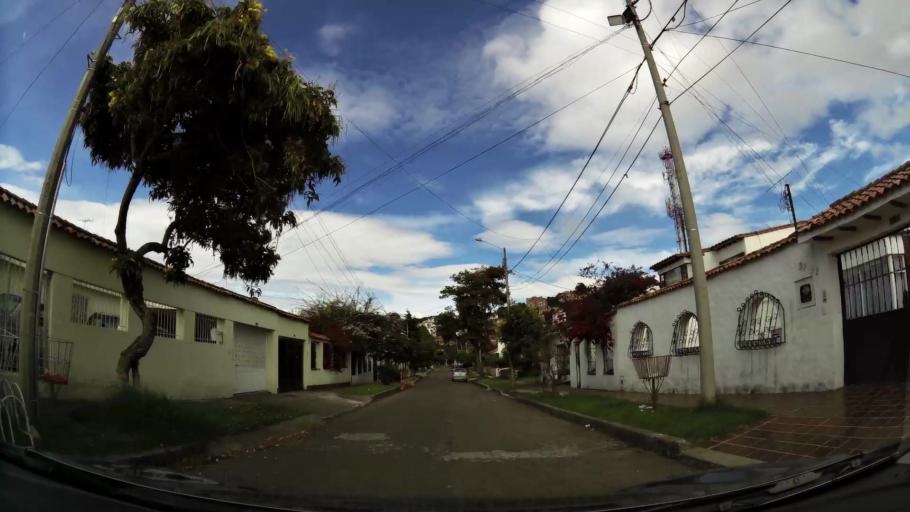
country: CO
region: Bogota D.C.
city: Barrio San Luis
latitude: 4.7126
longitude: -74.0765
